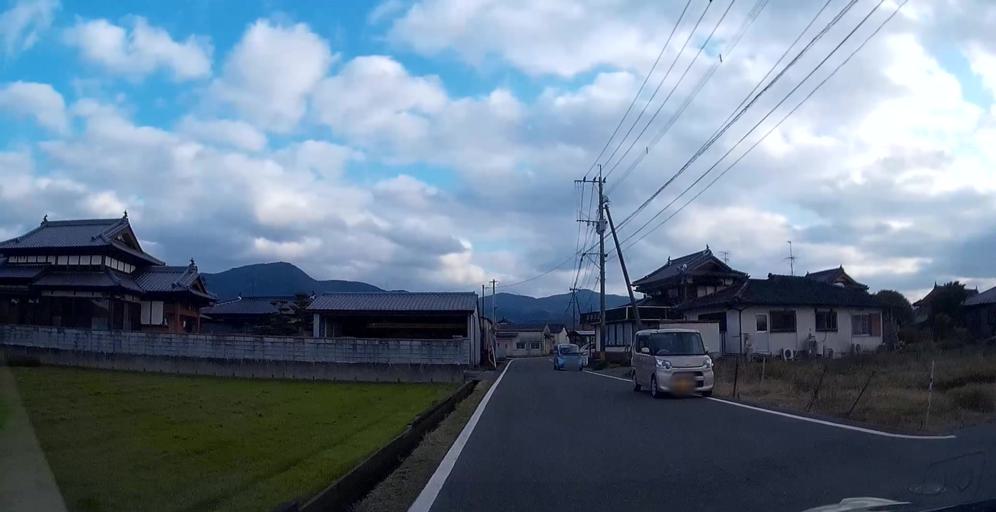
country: JP
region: Kumamoto
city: Yatsushiro
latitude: 32.5323
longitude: 130.6373
